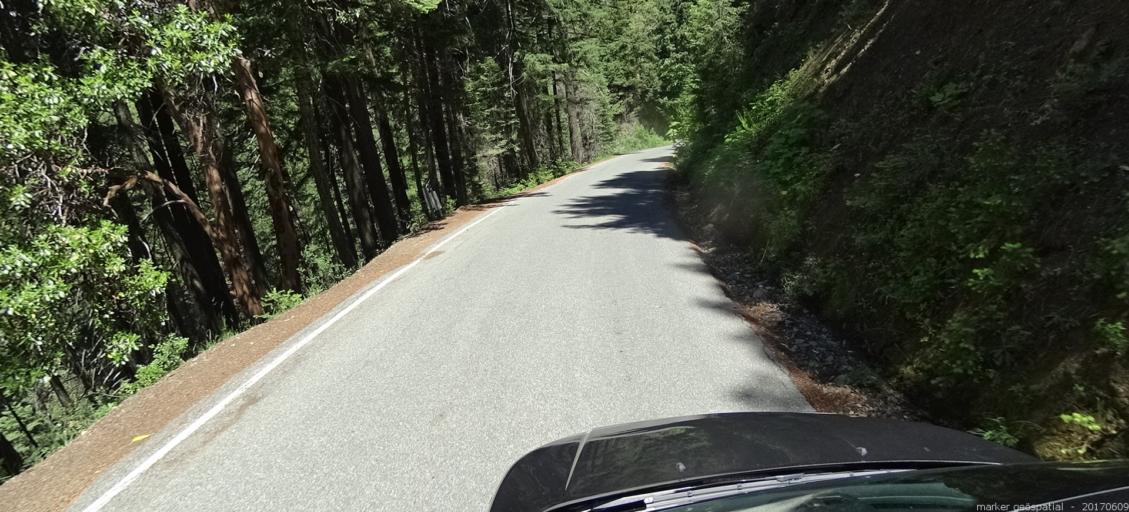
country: US
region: California
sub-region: Siskiyou County
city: Yreka
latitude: 41.3703
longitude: -123.0186
